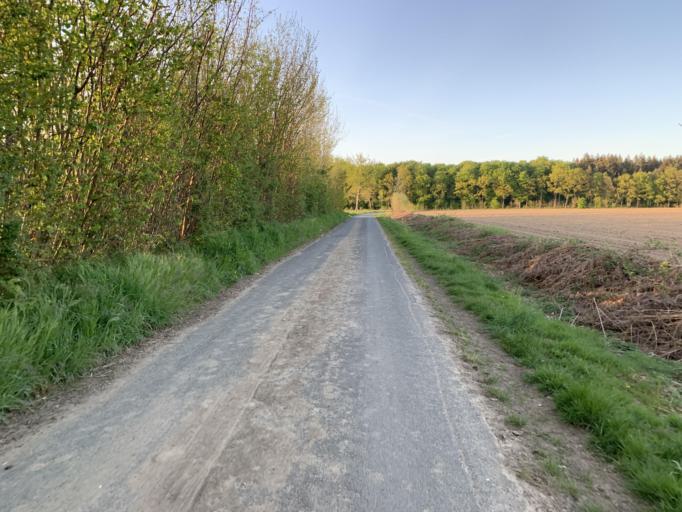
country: DE
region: Schleswig-Holstein
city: Worth
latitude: 53.4607
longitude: 10.4320
